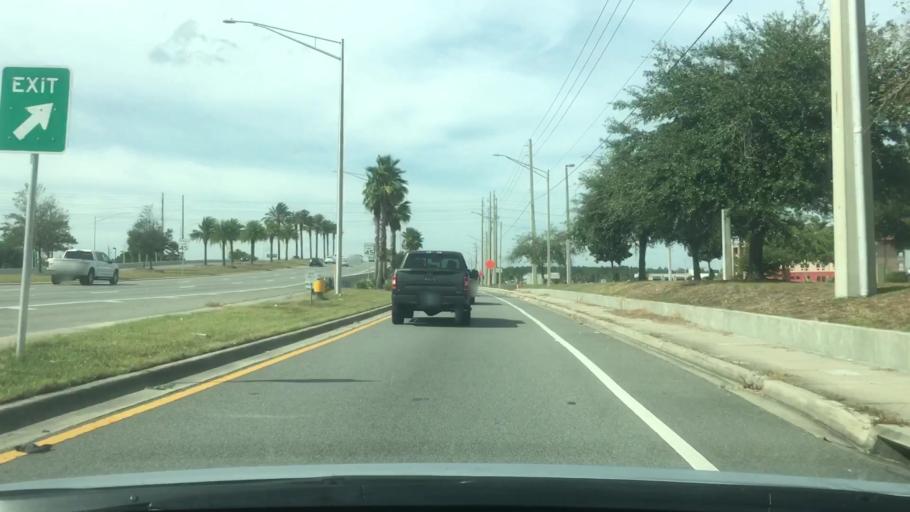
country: US
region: Florida
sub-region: Duval County
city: Atlantic Beach
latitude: 30.3192
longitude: -81.4856
